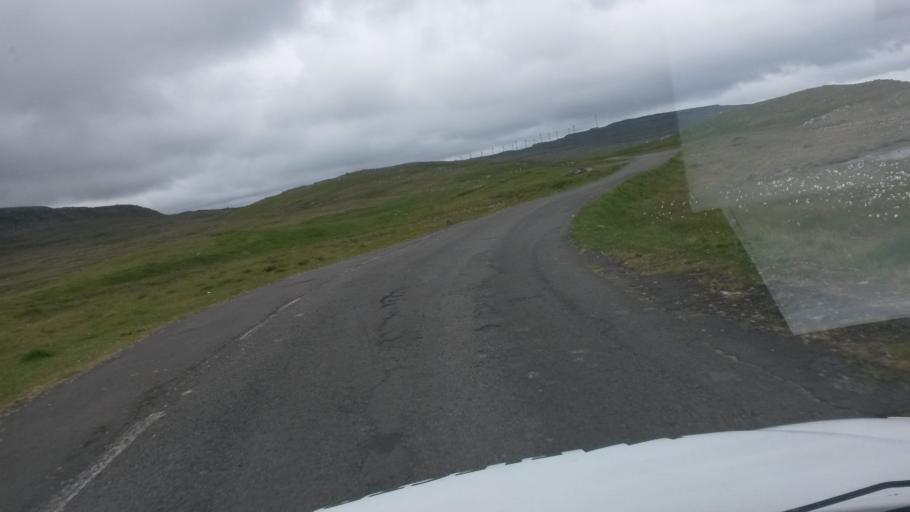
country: FO
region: Streymoy
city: Argir
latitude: 61.9928
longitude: -6.8490
